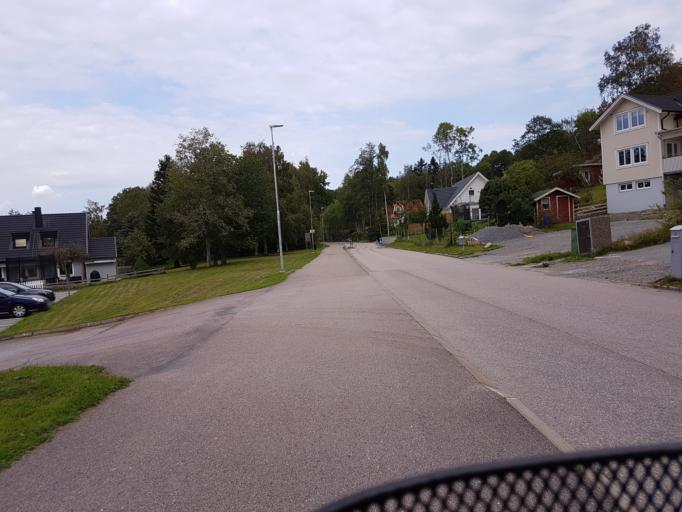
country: SE
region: Vaestra Goetaland
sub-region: Ale Kommun
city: Nodinge-Nol
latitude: 57.8972
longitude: 12.0563
